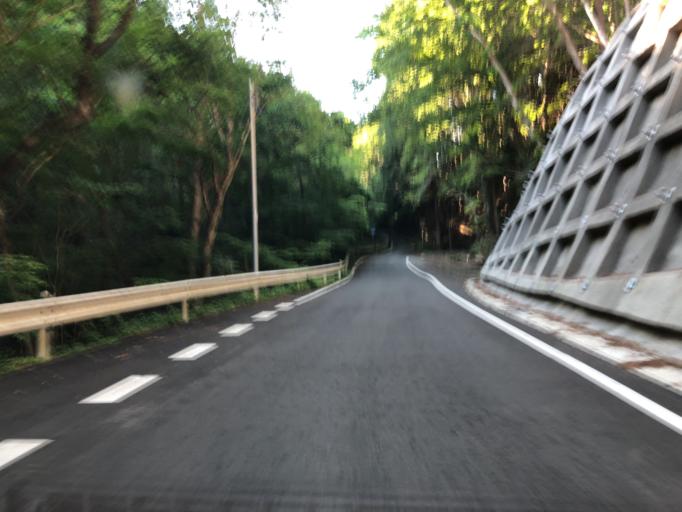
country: JP
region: Ibaraki
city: Kitaibaraki
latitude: 36.8948
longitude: 140.6208
